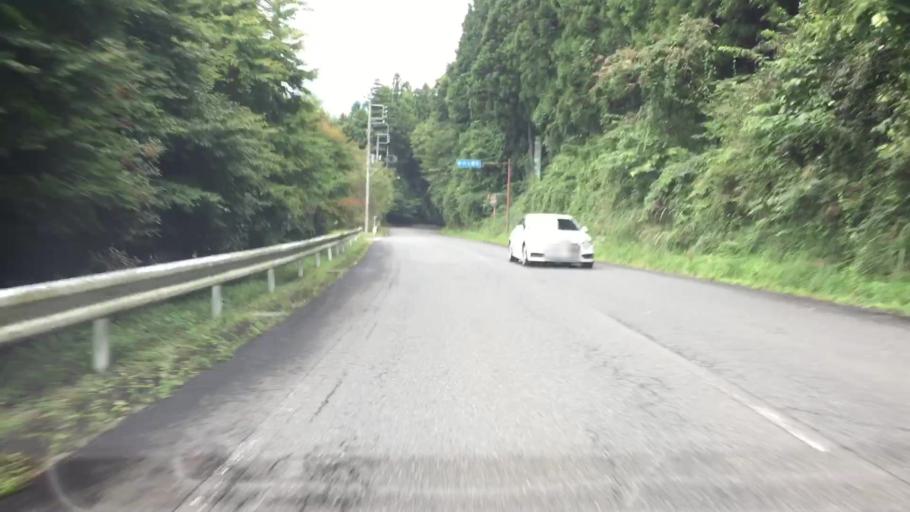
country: JP
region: Tochigi
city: Imaichi
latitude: 36.7552
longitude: 139.6854
